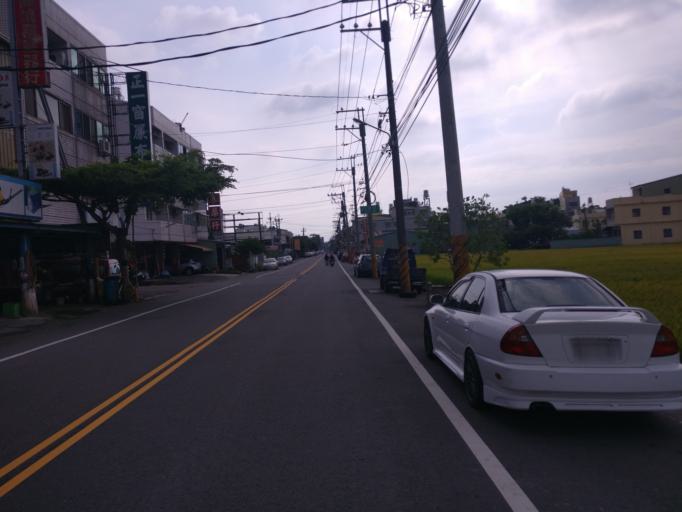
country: TW
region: Taiwan
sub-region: Taichung City
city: Taichung
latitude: 24.0659
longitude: 120.6880
